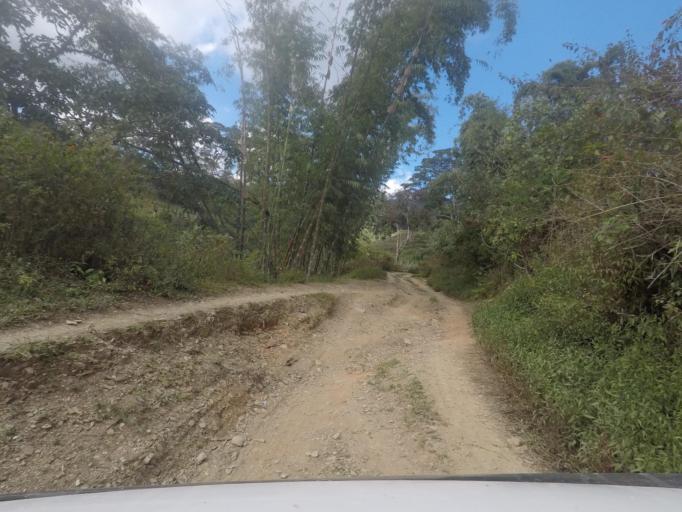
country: TL
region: Ermera
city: Gleno
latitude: -8.7490
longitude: 125.3230
